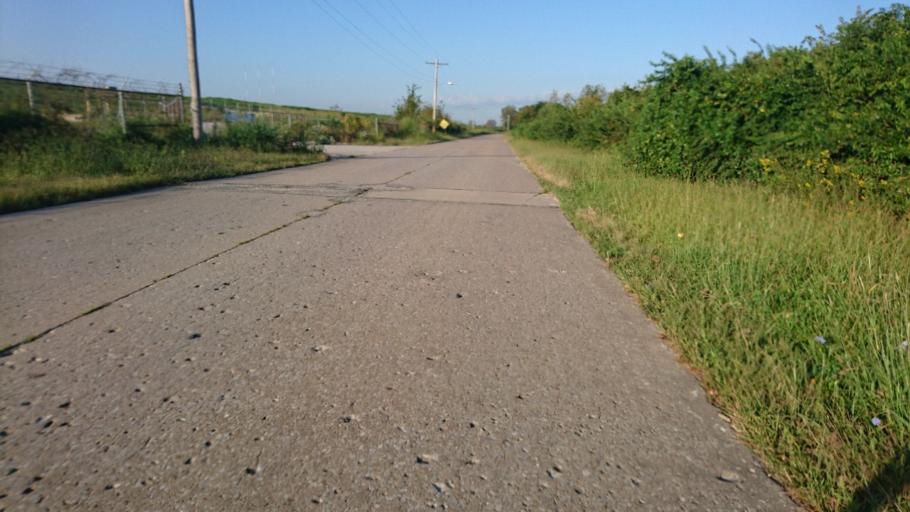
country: US
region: Missouri
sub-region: Saint Louis County
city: Glasgow Village
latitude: 38.7578
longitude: -90.1548
